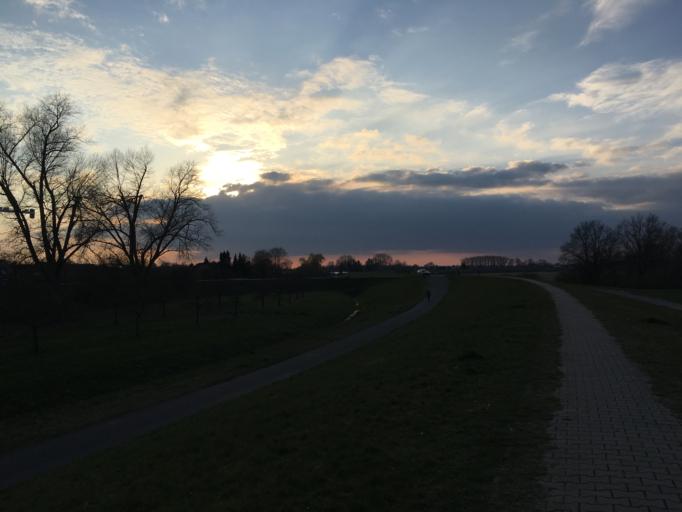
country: DE
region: Lower Saxony
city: Bleckede
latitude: 53.2976
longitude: 10.7287
